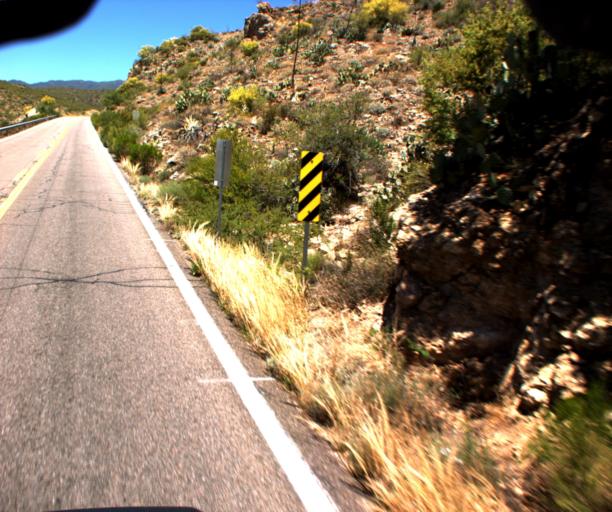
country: US
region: Arizona
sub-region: Pinal County
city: Kearny
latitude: 33.1800
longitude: -110.8114
